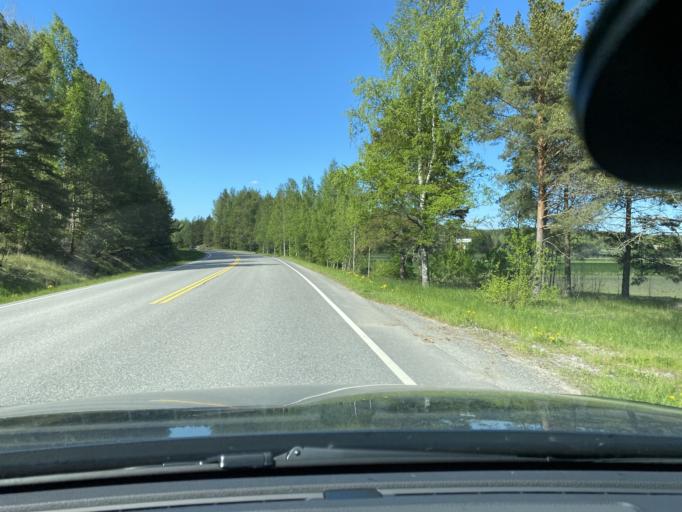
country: FI
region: Varsinais-Suomi
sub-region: Turku
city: Sauvo
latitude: 60.3653
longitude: 22.6743
